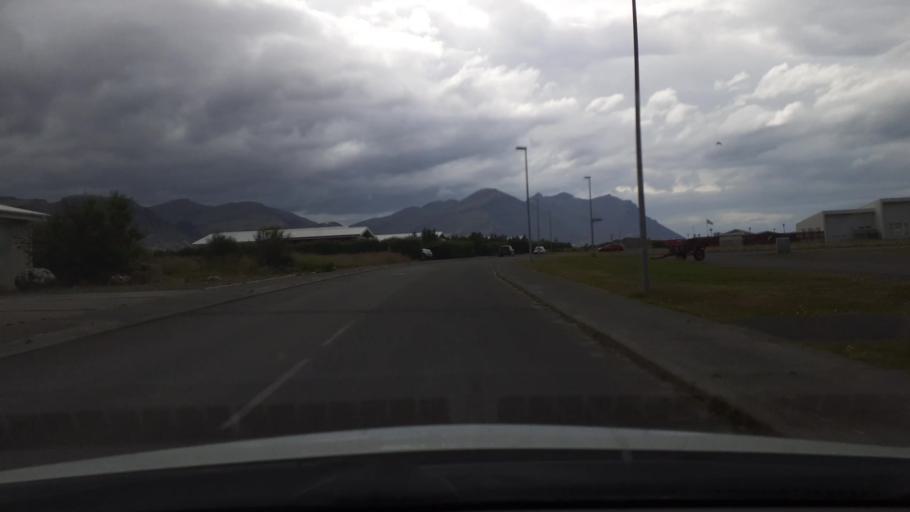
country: IS
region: West
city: Borgarnes
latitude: 64.5603
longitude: -21.7627
